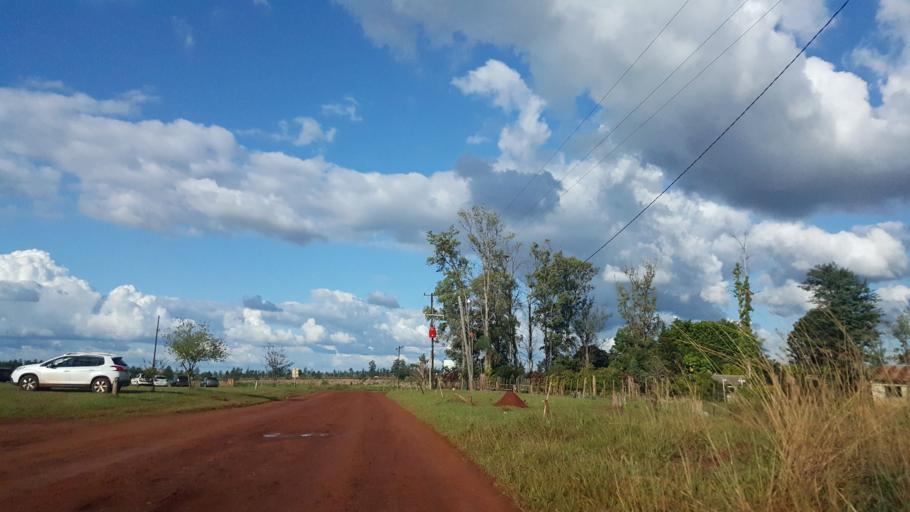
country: AR
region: Misiones
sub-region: Departamento de Capital
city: Posadas
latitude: -27.4187
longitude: -56.0028
